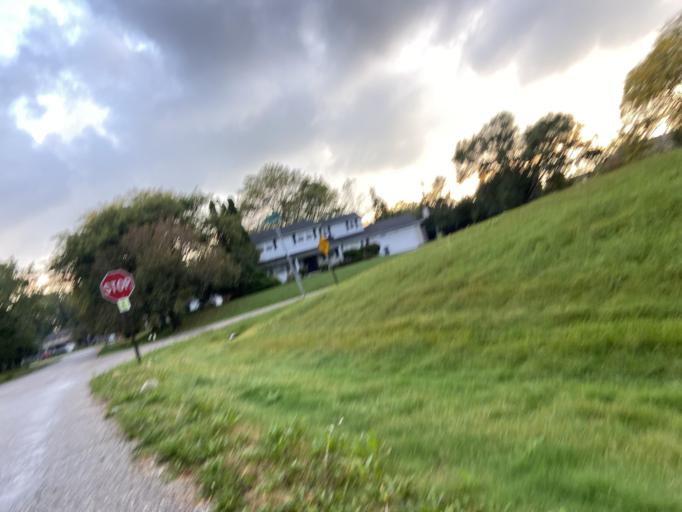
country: US
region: Michigan
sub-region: Oakland County
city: West Bloomfield Township
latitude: 42.5418
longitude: -83.3569
